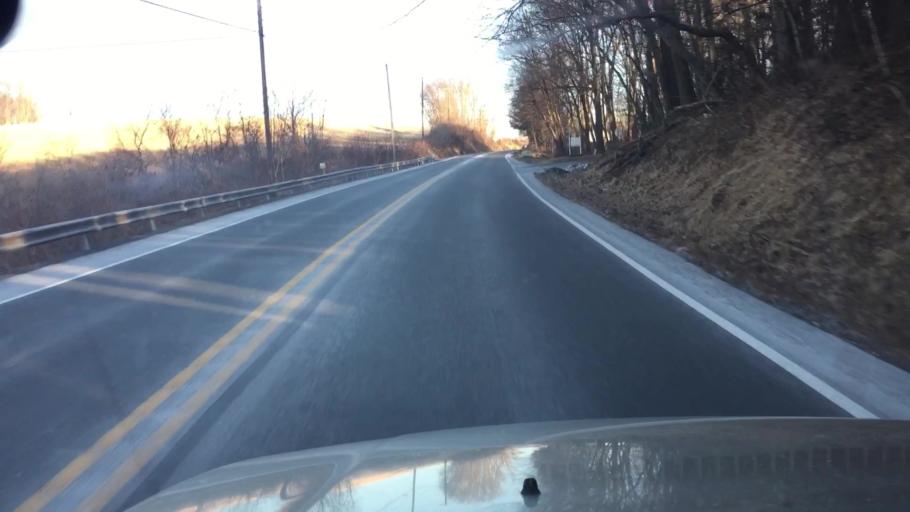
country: US
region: Pennsylvania
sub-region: Luzerne County
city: Nescopeck
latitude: 41.0533
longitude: -76.1710
